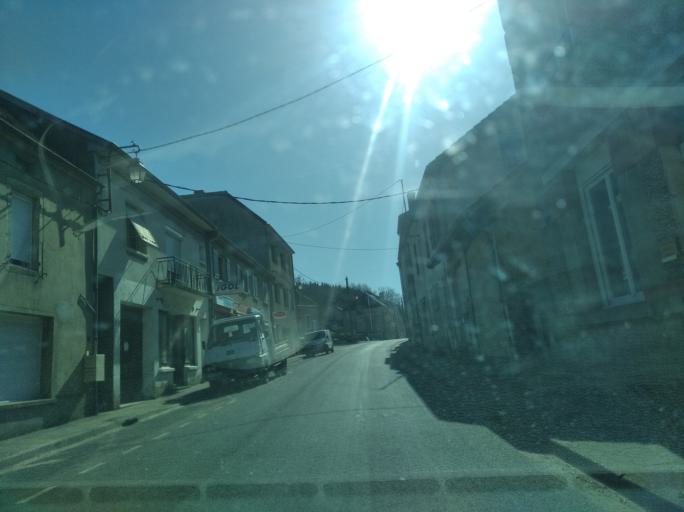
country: FR
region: Auvergne
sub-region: Departement de l'Allier
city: Le Mayet-de-Montagne
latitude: 46.0700
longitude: 3.6671
